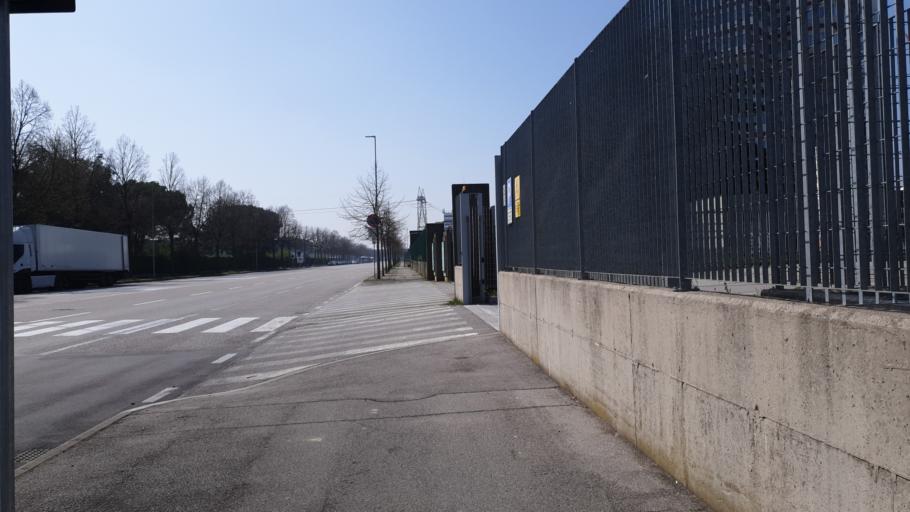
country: IT
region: Veneto
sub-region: Provincia di Padova
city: Ponte San Nicolo
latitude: 45.3932
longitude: 11.9316
